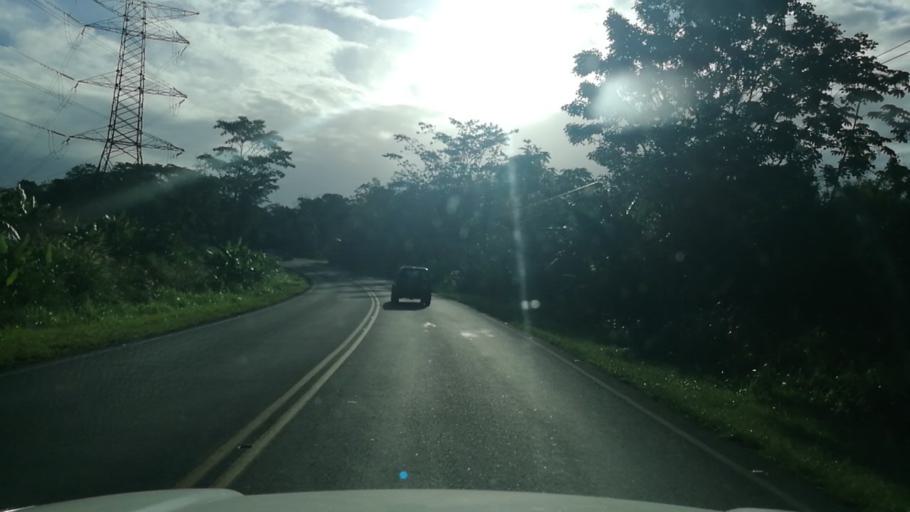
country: CR
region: Limon
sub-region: Canton de Matina
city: Batan
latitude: 10.0456
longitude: -83.3515
